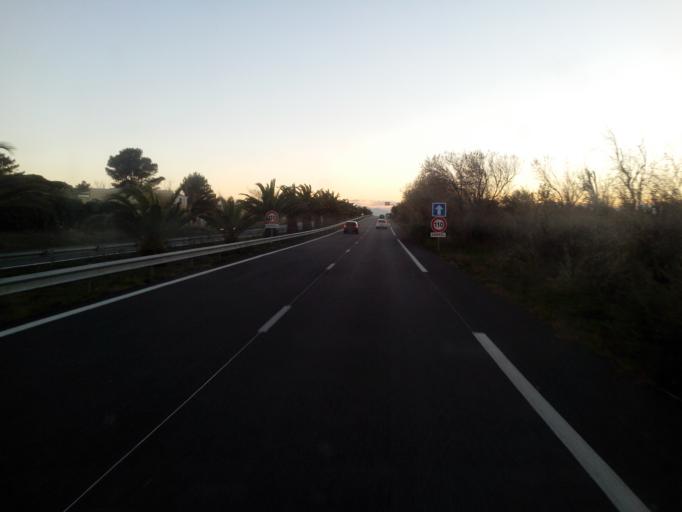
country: FR
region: Languedoc-Roussillon
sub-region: Departement des Pyrenees-Orientales
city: Le Barcares
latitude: 42.8289
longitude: 3.0346
